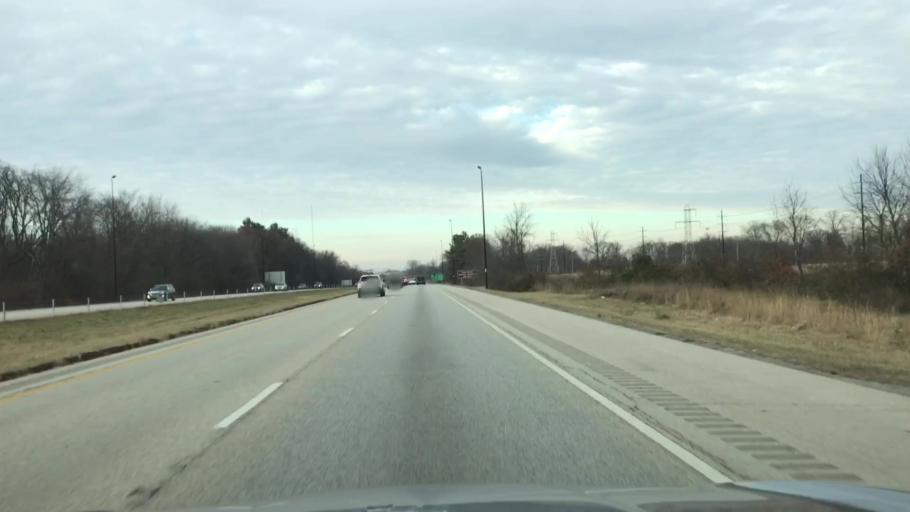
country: US
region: Illinois
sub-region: Sangamon County
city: Grandview
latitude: 39.8138
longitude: -89.5928
